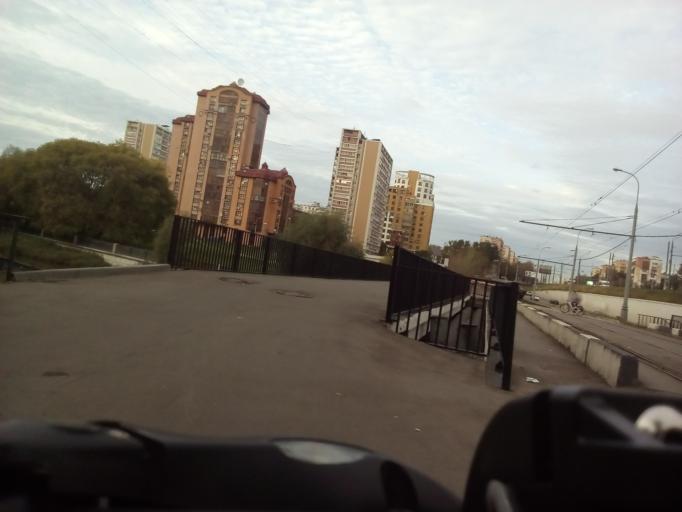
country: RU
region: Moscow
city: Rostokino
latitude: 55.8336
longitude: 37.6536
